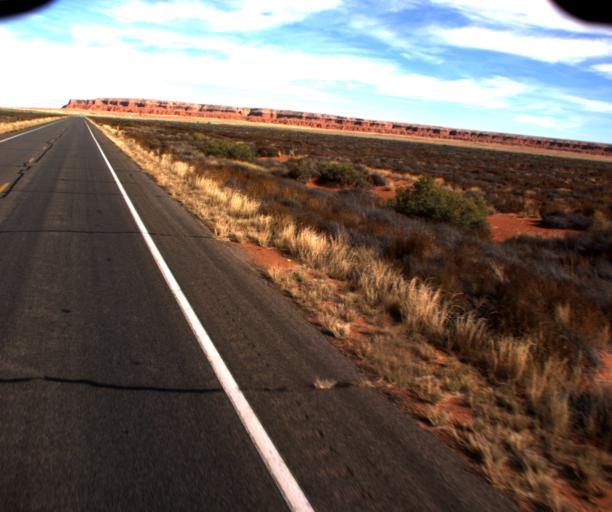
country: US
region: Arizona
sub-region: Navajo County
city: Kayenta
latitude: 36.7820
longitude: -109.9834
